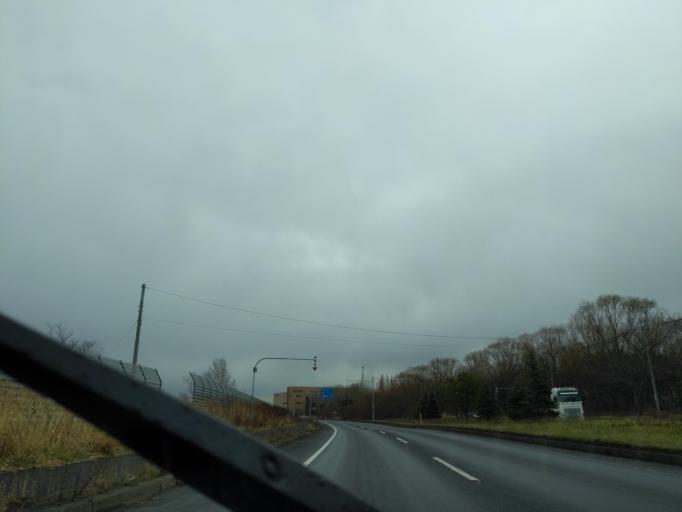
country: JP
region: Hokkaido
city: Ishikari
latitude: 43.1680
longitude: 141.4049
